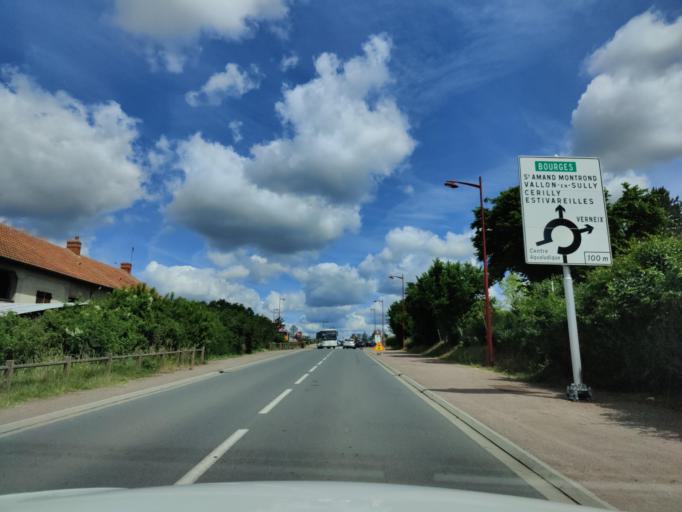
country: FR
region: Auvergne
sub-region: Departement de l'Allier
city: Saint-Victor
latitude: 46.3984
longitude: 2.6097
